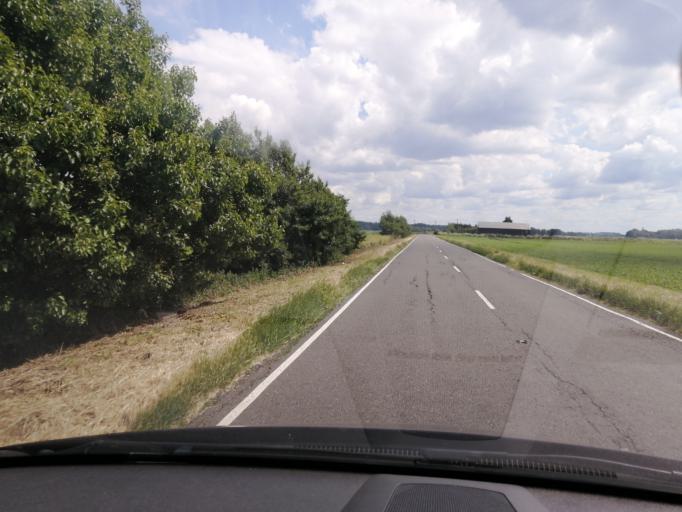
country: GB
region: England
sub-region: Cambridgeshire
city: Yaxley
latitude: 52.5004
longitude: -0.2502
